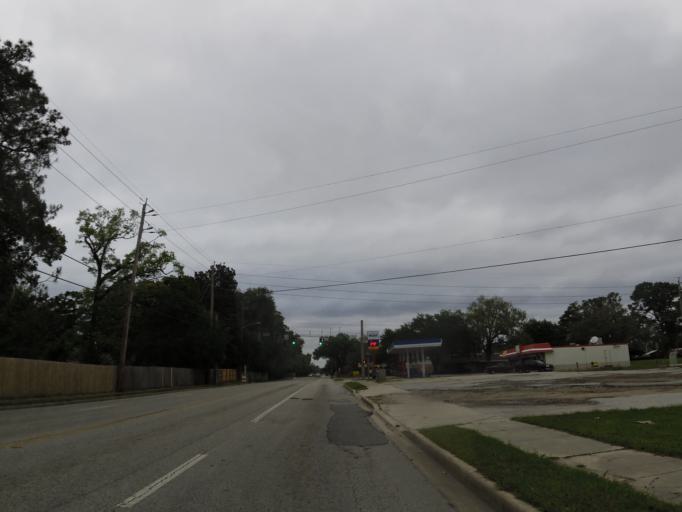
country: US
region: Florida
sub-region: Duval County
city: Jacksonville
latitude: 30.2671
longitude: -81.6330
